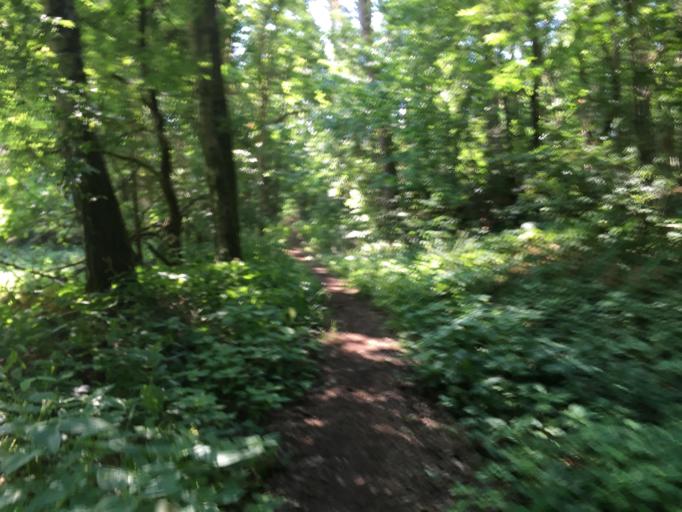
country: DE
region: Brandenburg
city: Templin
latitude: 53.1241
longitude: 13.5676
